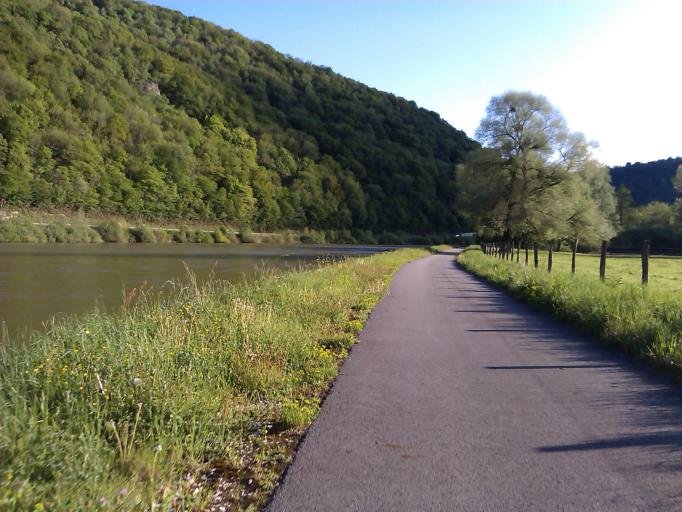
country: FR
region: Franche-Comte
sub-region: Departement du Doubs
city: Clerval
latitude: 47.3995
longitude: 6.5077
